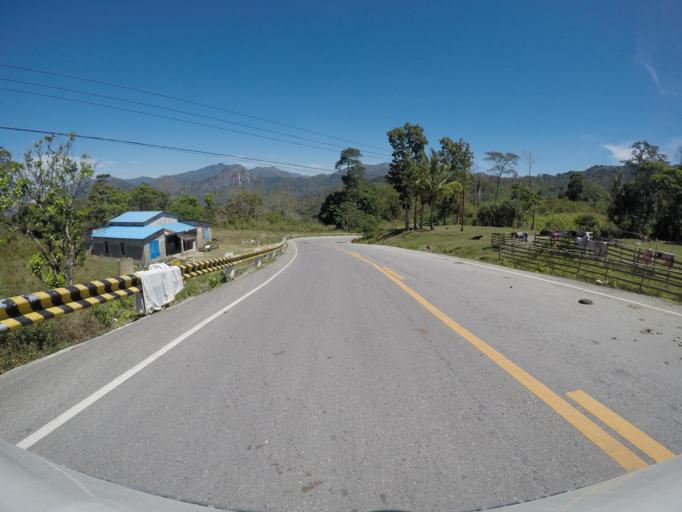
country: TL
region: Manatuto
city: Manatuto
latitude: -8.8246
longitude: 125.9804
